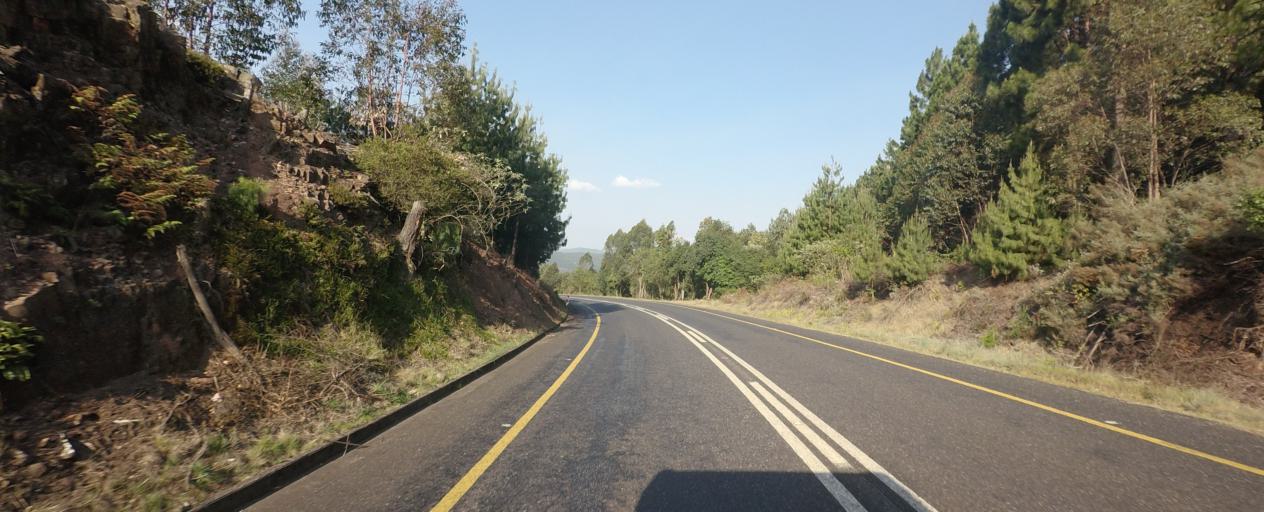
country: ZA
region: Mpumalanga
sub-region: Ehlanzeni District
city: Lydenburg
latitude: -25.1776
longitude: 30.6540
